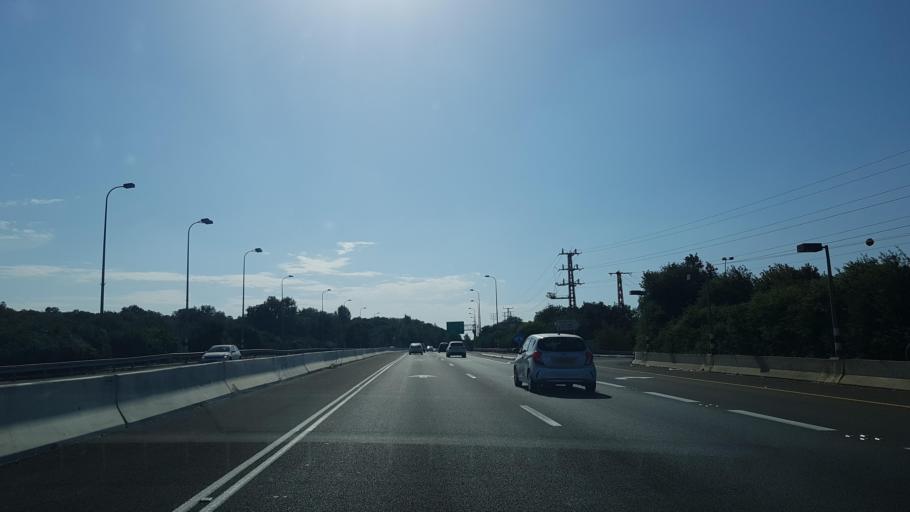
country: IL
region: Northern District
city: Bir el Maksur
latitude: 32.7674
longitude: 35.2514
